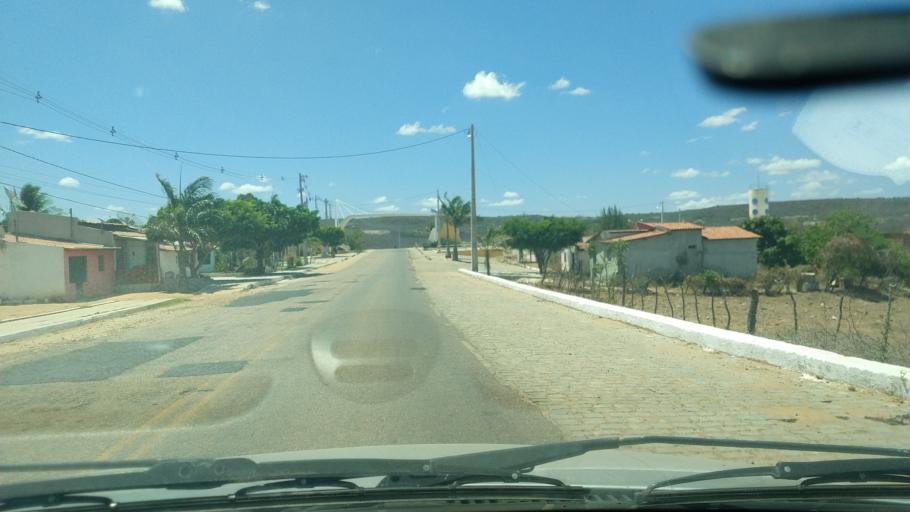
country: BR
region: Rio Grande do Norte
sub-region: Cerro Cora
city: Cerro Cora
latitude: -6.0562
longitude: -36.3589
